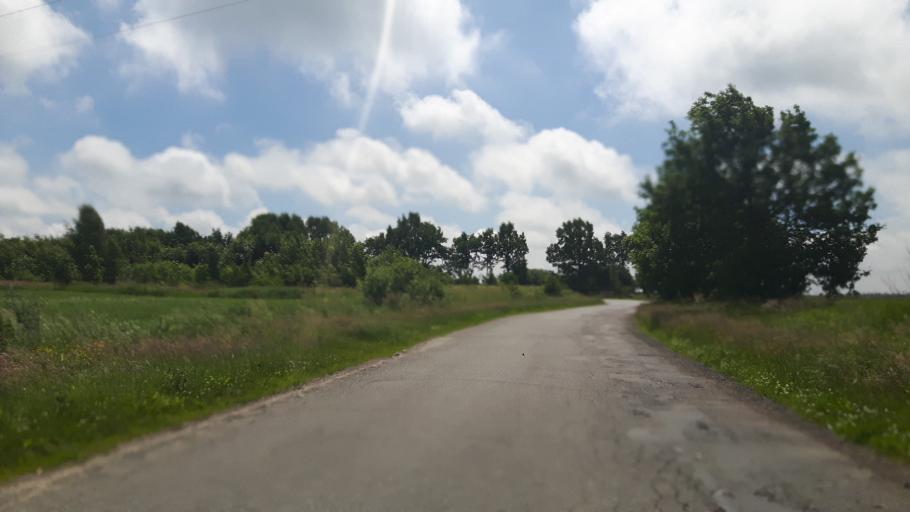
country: PL
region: West Pomeranian Voivodeship
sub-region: Powiat slawienski
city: Slawno
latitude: 54.5071
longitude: 16.6235
